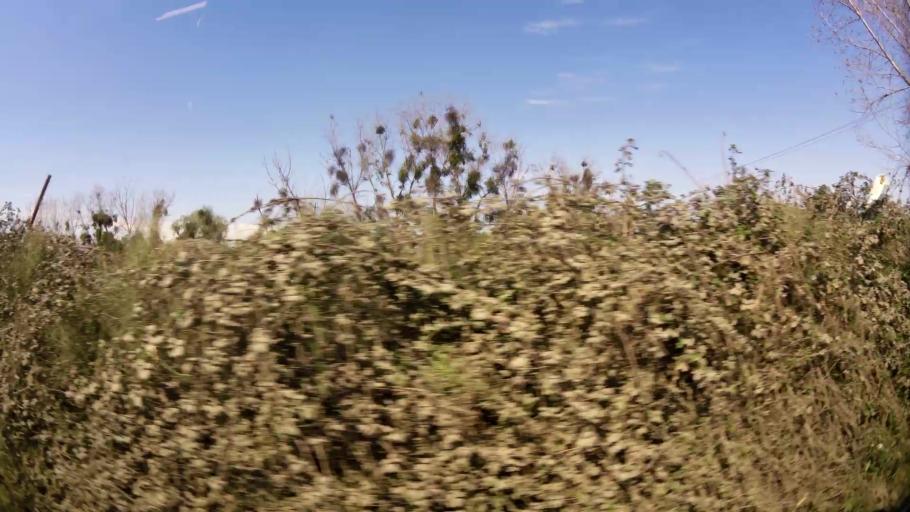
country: CL
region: Santiago Metropolitan
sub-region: Provincia de Talagante
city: Penaflor
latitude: -33.5932
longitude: -70.8794
